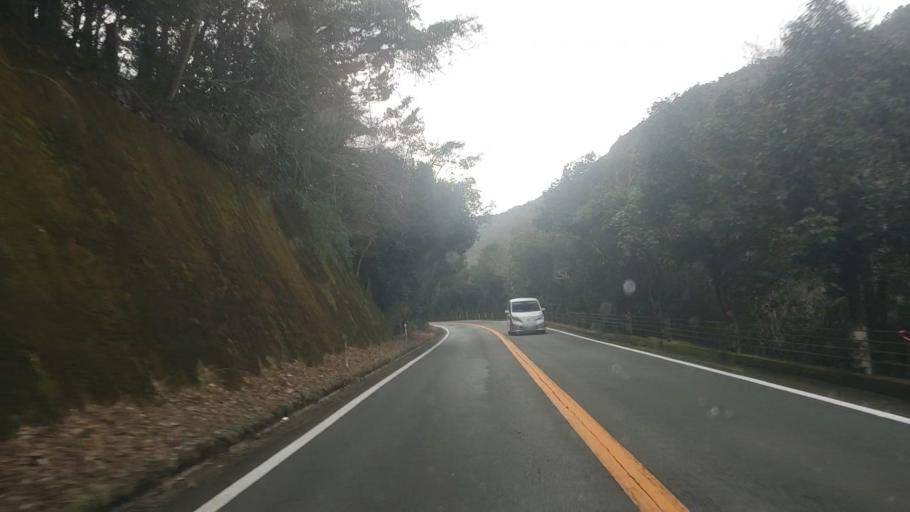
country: JP
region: Kumamoto
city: Hitoyoshi
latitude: 32.1266
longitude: 130.8137
